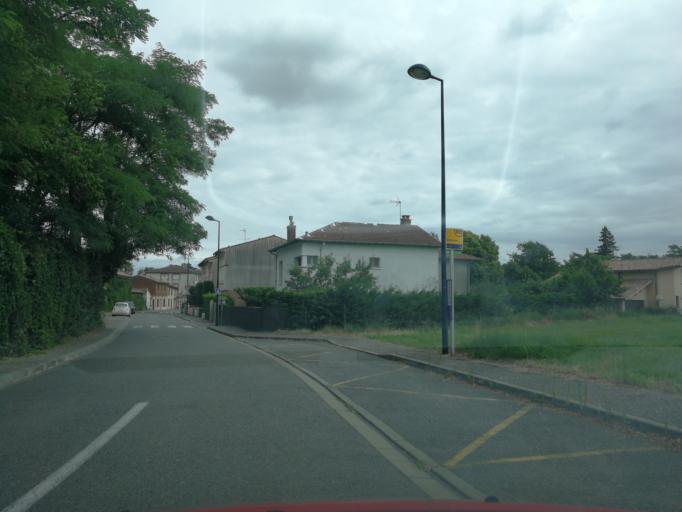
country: FR
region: Midi-Pyrenees
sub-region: Departement de la Haute-Garonne
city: Auzeville-Tolosane
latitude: 43.5316
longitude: 1.4773
